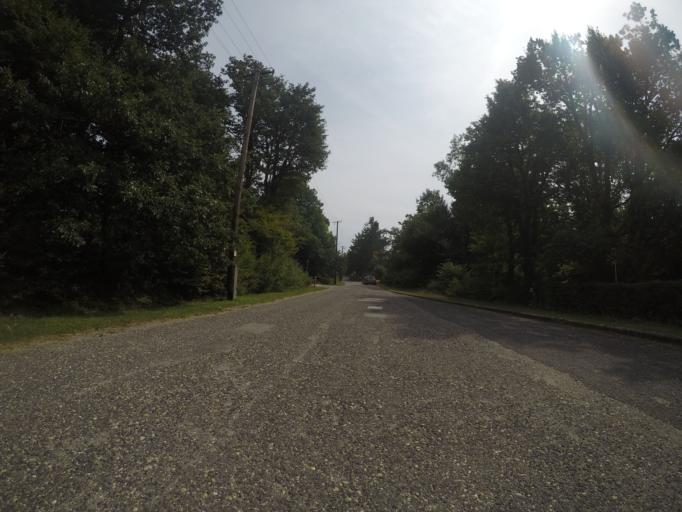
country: HU
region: Pest
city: Pilisszentkereszt
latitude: 47.7185
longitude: 18.8953
